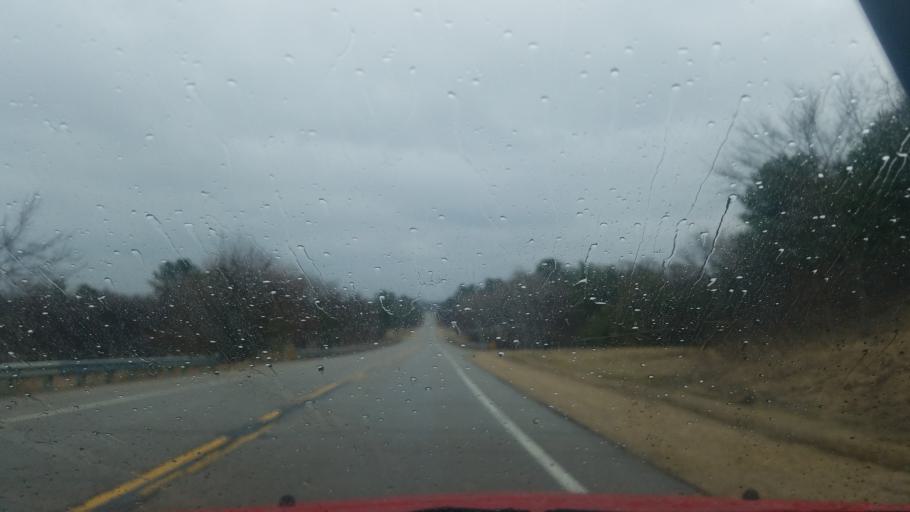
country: US
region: Wisconsin
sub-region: Dunn County
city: Menomonie
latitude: 44.9485
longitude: -91.9125
